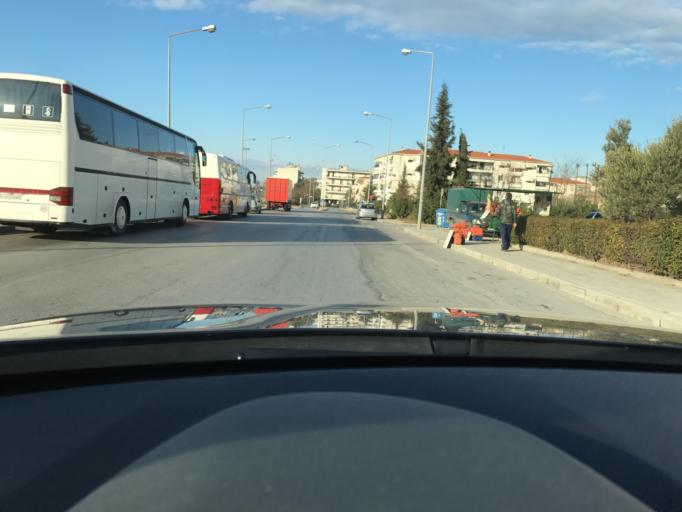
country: GR
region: Central Macedonia
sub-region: Nomos Thessalonikis
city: Efkarpia
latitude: 40.6801
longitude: 22.9546
